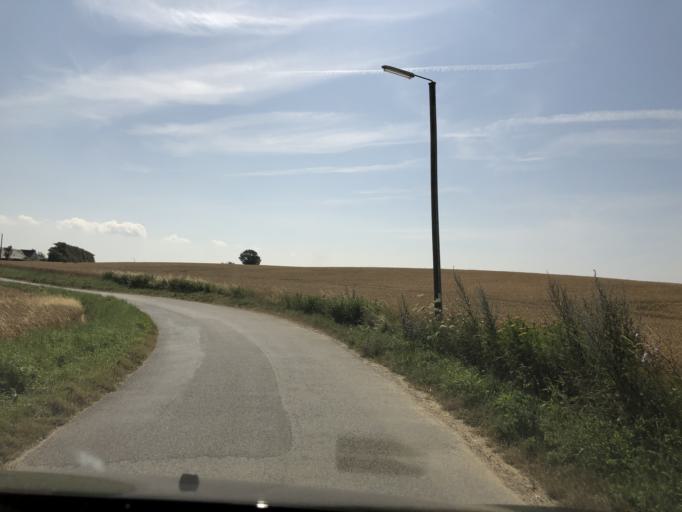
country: DK
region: South Denmark
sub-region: Faaborg-Midtfyn Kommune
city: Faaborg
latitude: 54.9465
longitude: 10.2372
